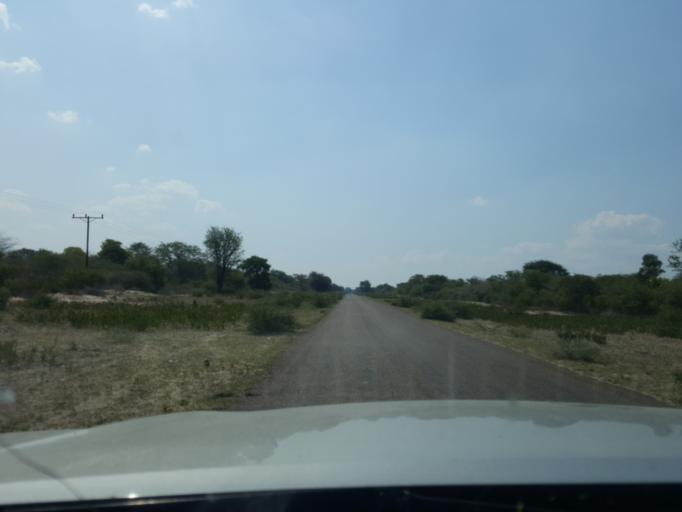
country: BW
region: North West
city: Shakawe
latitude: -18.8865
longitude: 22.2666
